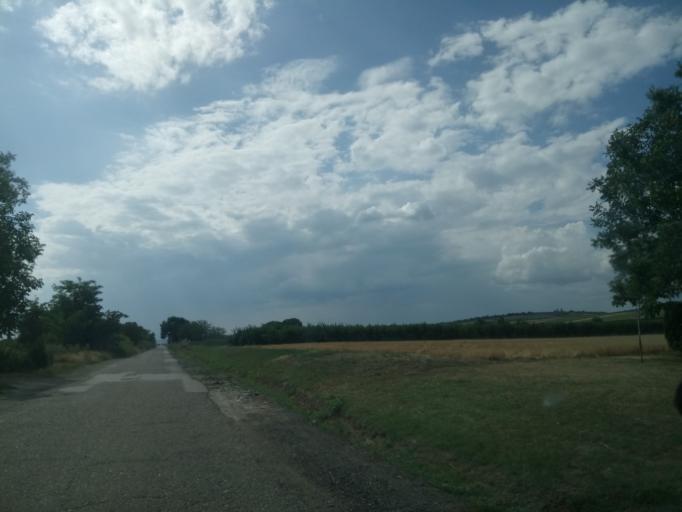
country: RS
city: Novi Slankamen
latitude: 45.1357
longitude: 20.2406
